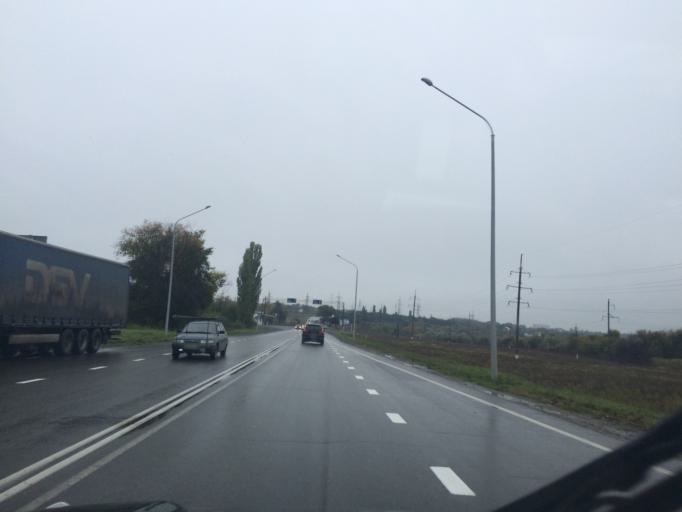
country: RU
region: Rostov
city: Azov
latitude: 47.0846
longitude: 39.4839
